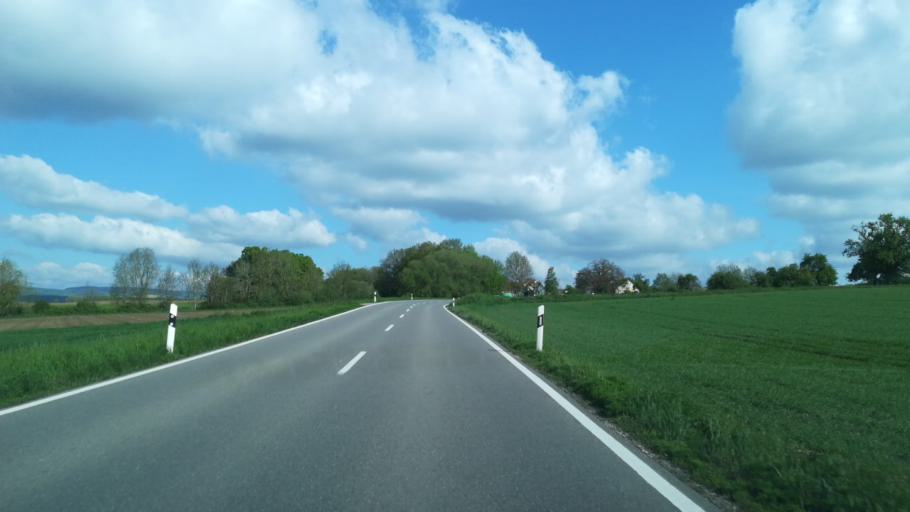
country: CH
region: Schaffhausen
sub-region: Bezirk Reiat
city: Thayngen
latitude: 47.7733
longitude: 8.7261
